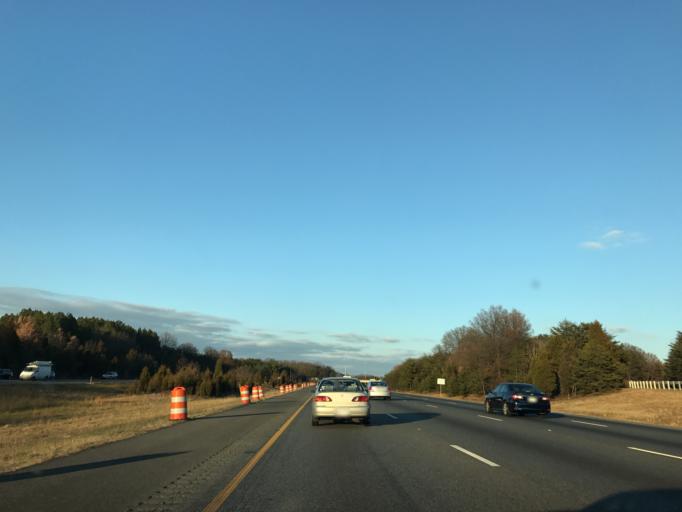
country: US
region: Maryland
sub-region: Howard County
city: North Laurel
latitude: 39.1244
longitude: -76.8654
